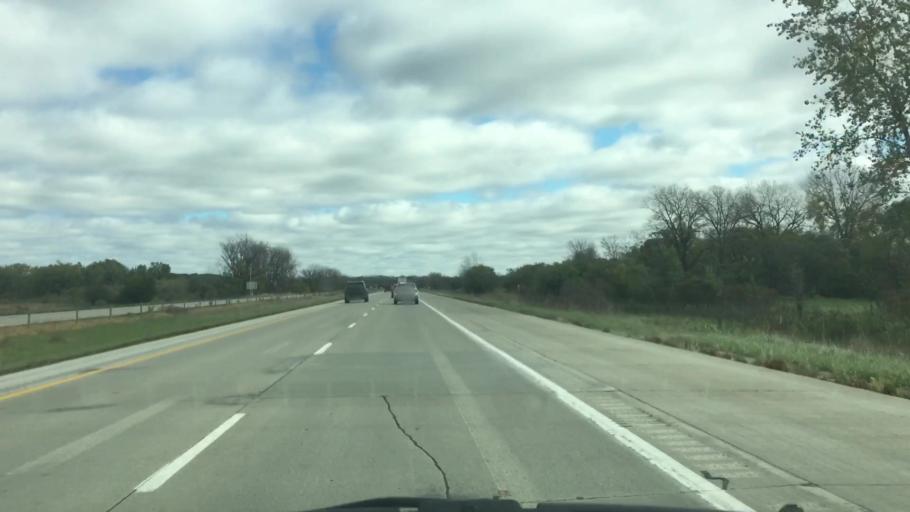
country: US
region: Iowa
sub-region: Polk County
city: Mitchellville
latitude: 41.6816
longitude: -93.3128
